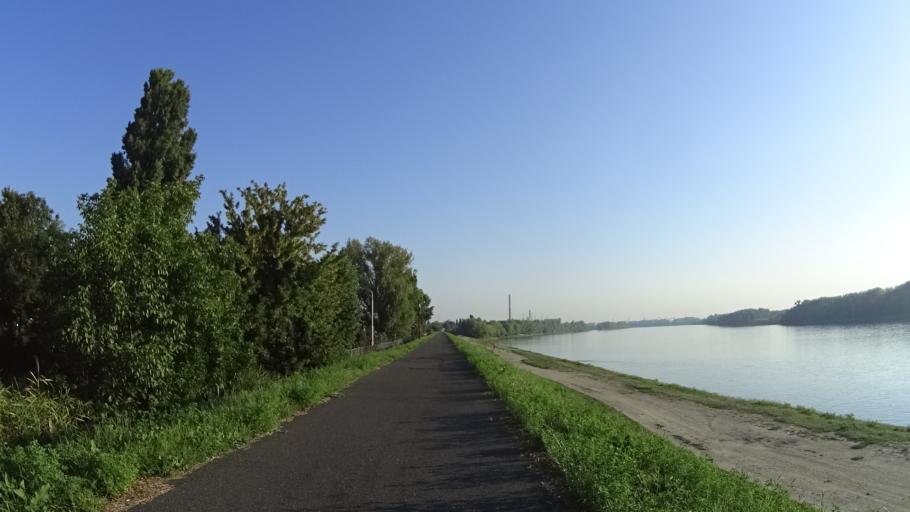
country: HU
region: Budapest
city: Budapest XXII. keruelet
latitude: 47.4429
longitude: 19.0491
